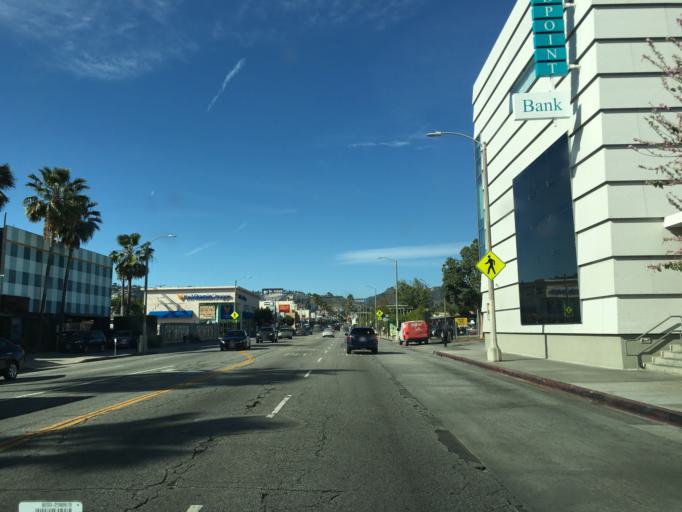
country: US
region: California
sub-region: Los Angeles County
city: West Hollywood
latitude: 34.0734
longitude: -118.3613
